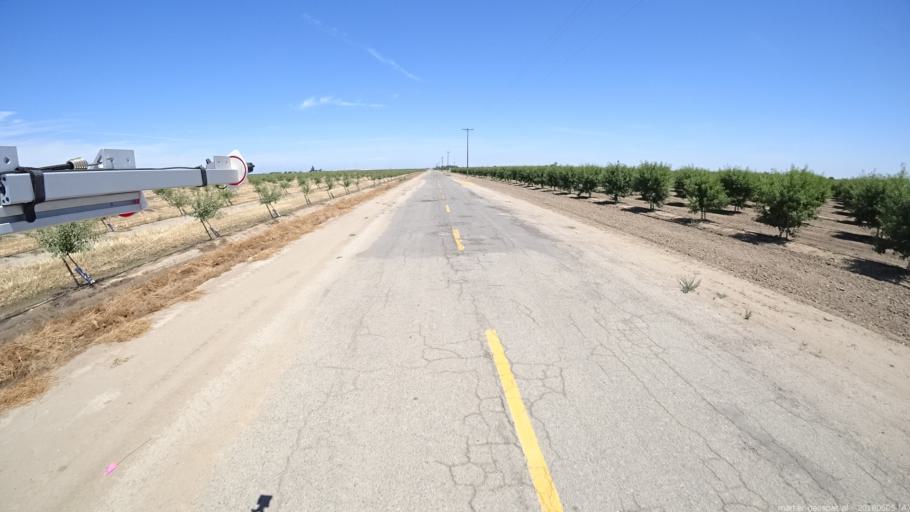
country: US
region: California
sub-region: Madera County
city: Chowchilla
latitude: 37.0906
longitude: -120.3729
